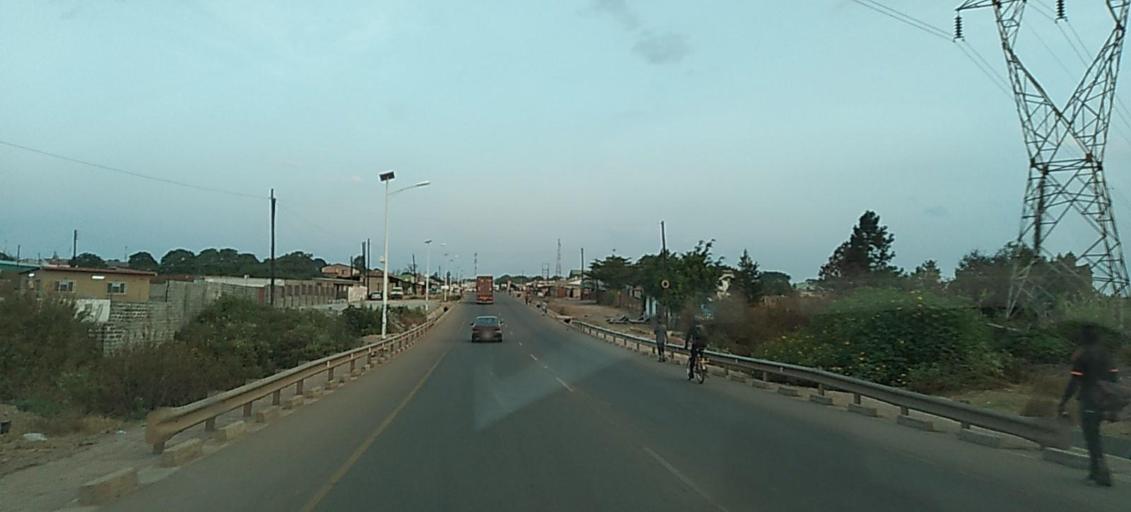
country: ZM
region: Copperbelt
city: Chingola
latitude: -12.5441
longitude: 27.8484
